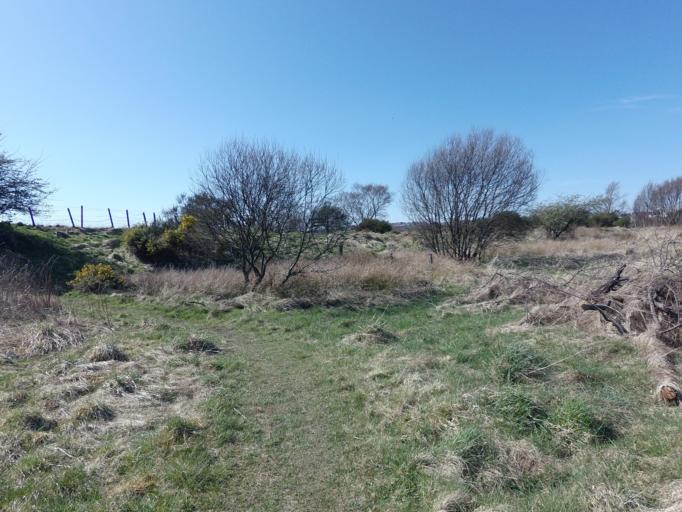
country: GB
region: Scotland
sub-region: West Lothian
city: West Calder
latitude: 55.8927
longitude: -3.5825
